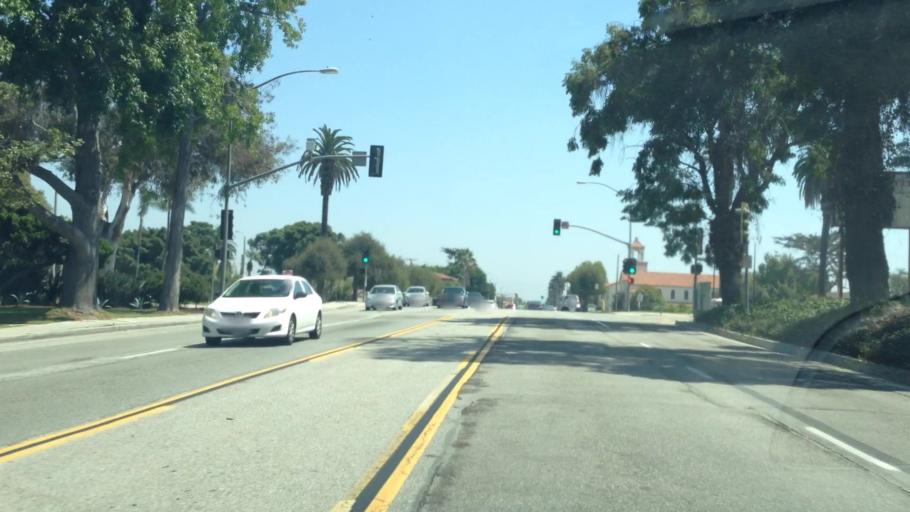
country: US
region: California
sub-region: Los Angeles County
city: Torrance
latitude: 33.8313
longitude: -118.3218
